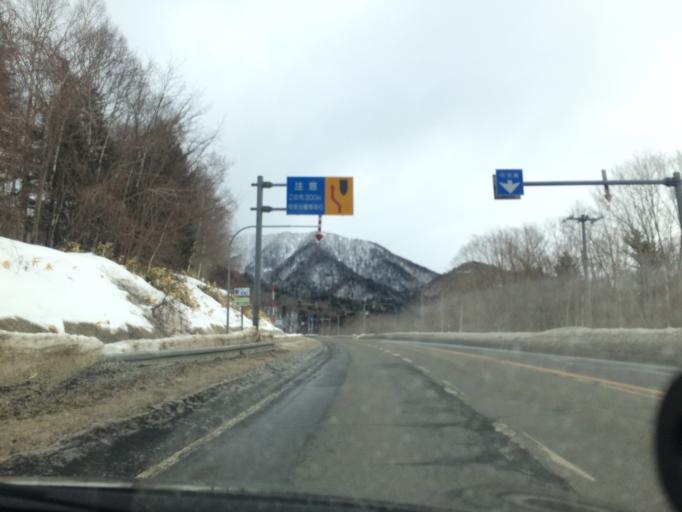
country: JP
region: Hokkaido
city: Shimo-furano
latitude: 42.8818
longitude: 142.2779
